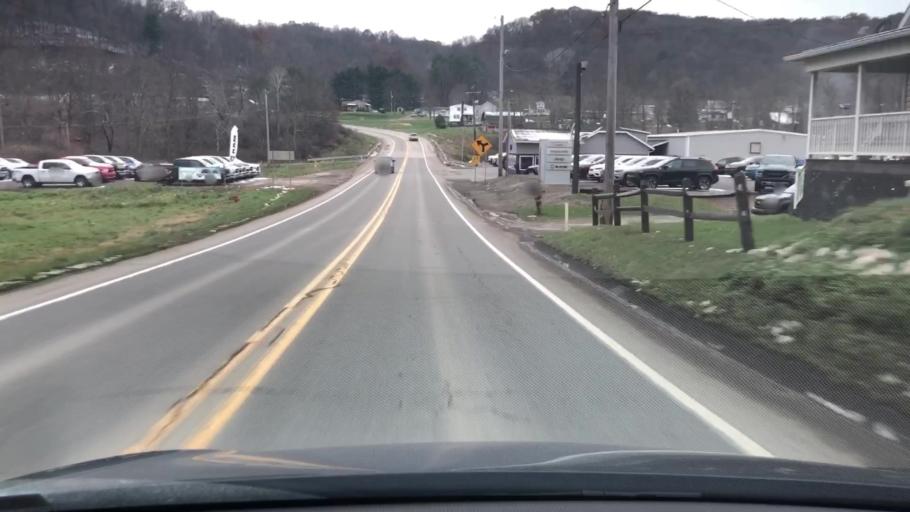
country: US
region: Pennsylvania
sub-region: Clarion County
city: Clarion
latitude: 41.0147
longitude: -79.2974
